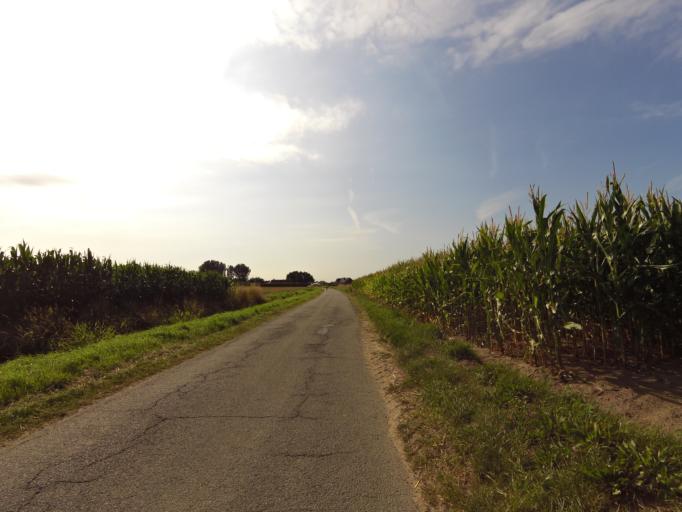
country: BE
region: Flanders
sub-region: Provincie West-Vlaanderen
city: Jabbeke
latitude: 51.1781
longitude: 3.0653
